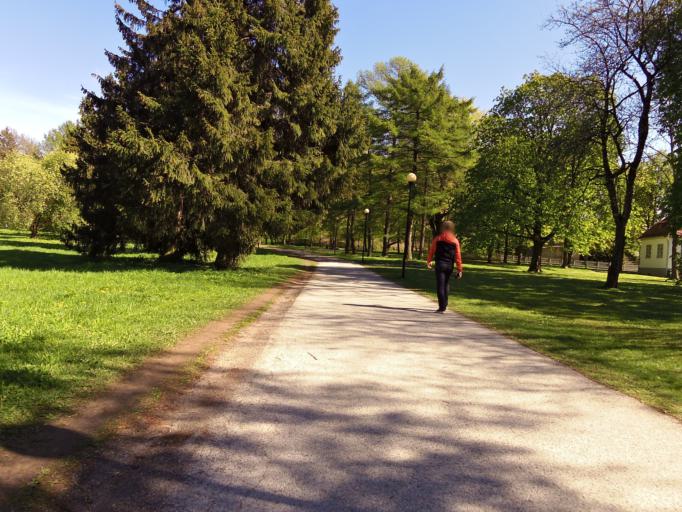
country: EE
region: Harju
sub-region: Tallinna linn
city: Tallinn
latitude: 59.4383
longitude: 24.7959
